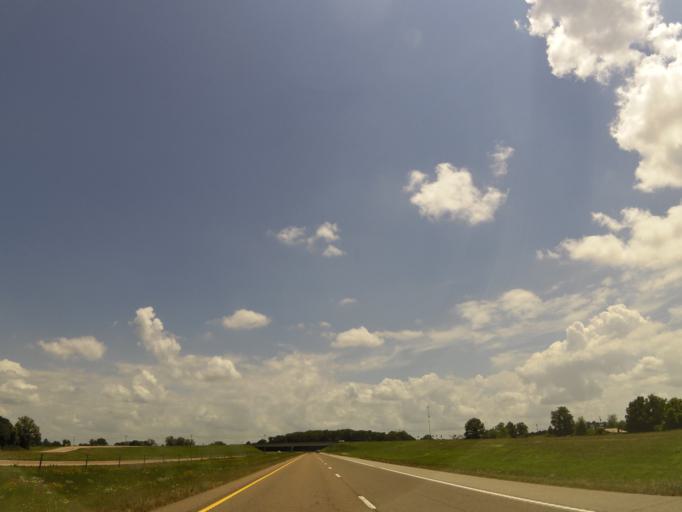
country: US
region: Tennessee
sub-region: Crockett County
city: Alamo
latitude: 35.8008
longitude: -89.1601
